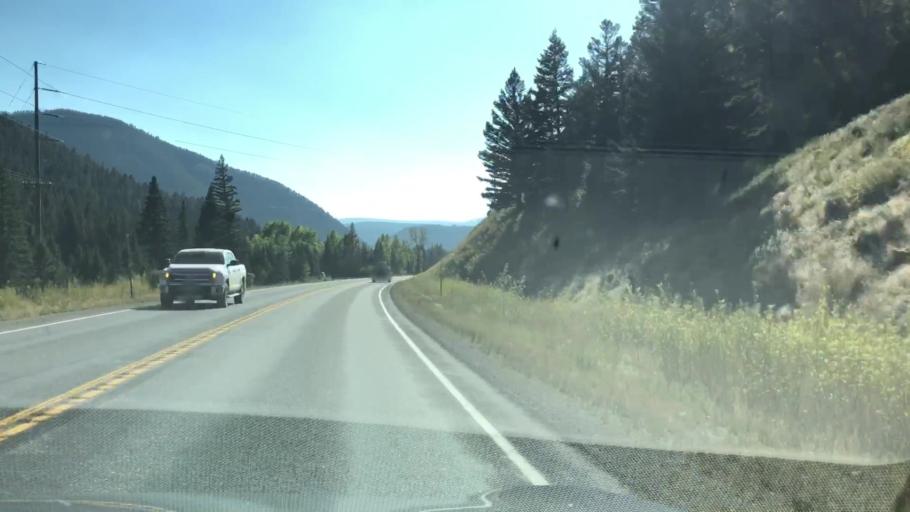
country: US
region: Montana
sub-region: Gallatin County
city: Big Sky
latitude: 45.2801
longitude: -111.2274
